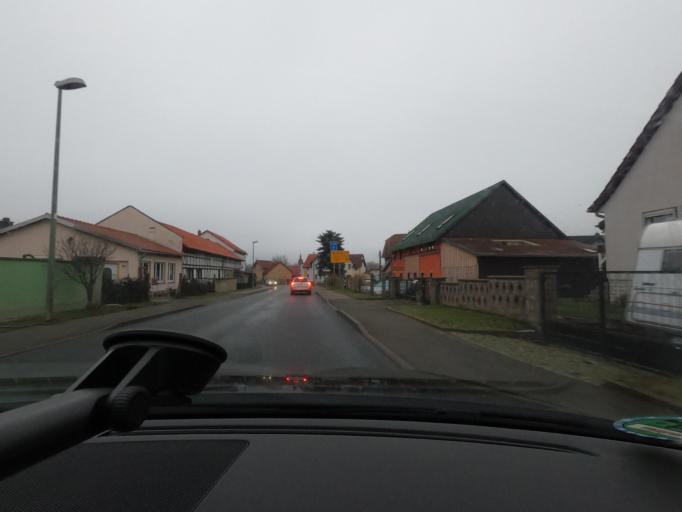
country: DE
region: Thuringia
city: Dornheim
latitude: 50.8221
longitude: 11.0124
